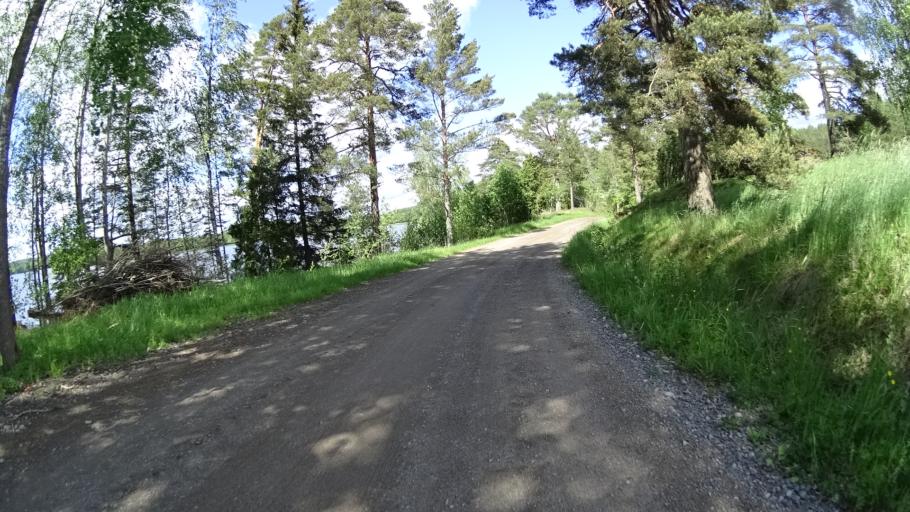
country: FI
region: Uusimaa
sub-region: Raaseporin
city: Karis
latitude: 60.1287
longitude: 23.6157
